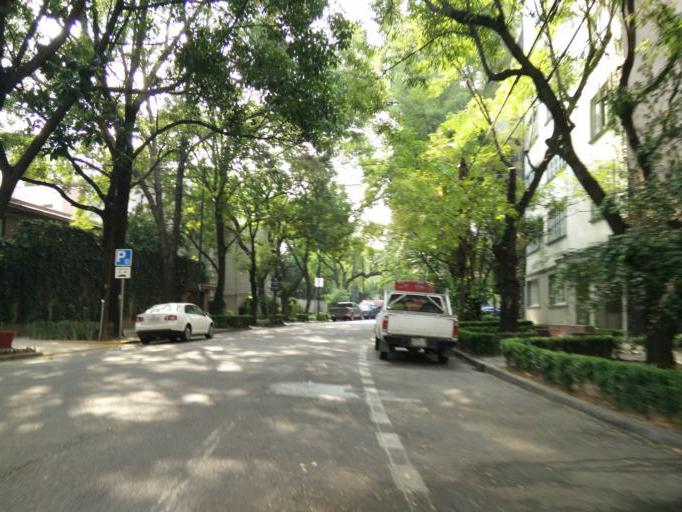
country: MX
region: Mexico City
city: Miguel Hidalgo
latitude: 19.4304
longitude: -99.1872
